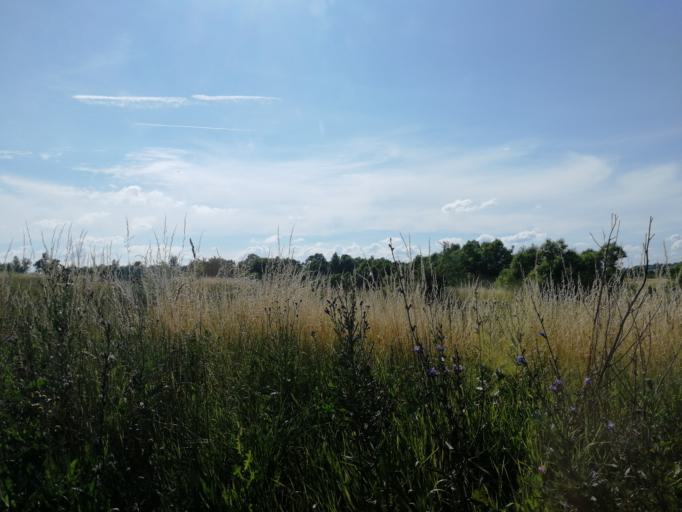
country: RU
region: Tula
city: Tovarkovskiy
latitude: 53.6055
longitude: 38.2720
